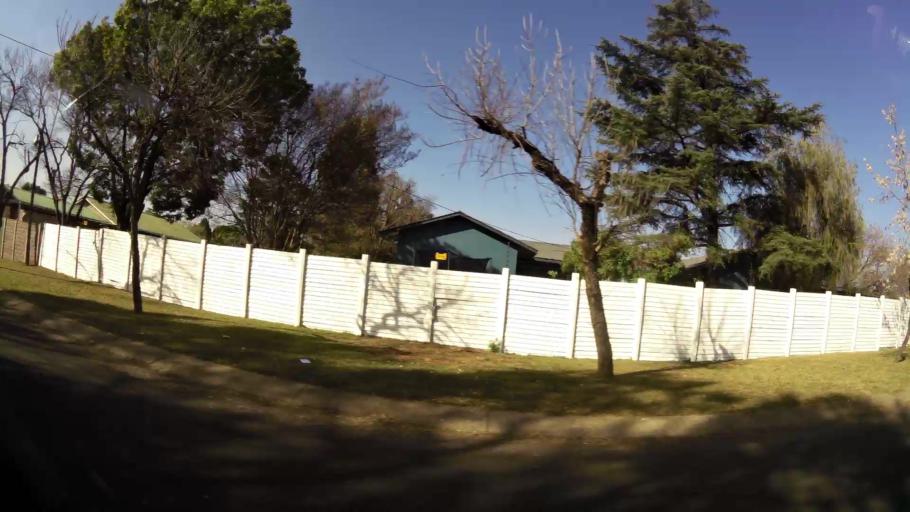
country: ZA
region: Gauteng
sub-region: City of Tshwane Metropolitan Municipality
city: Pretoria
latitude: -25.7257
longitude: 28.2480
